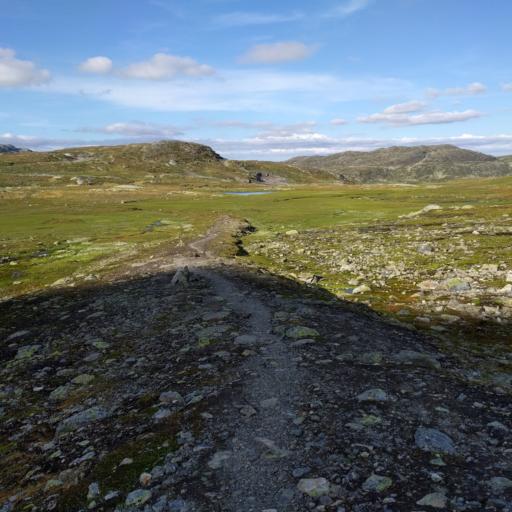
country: NO
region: Aust-Agder
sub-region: Bykle
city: Hovden
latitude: 59.9297
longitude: 7.2165
